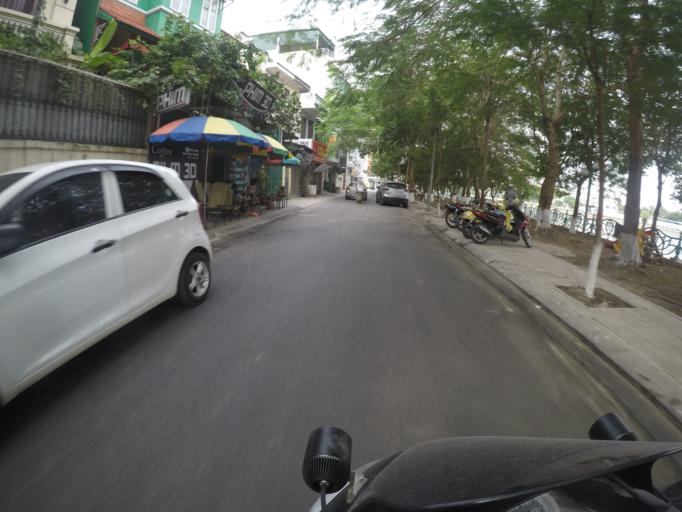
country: VN
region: Ha Noi
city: Tay Ho
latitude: 21.0721
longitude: 105.8144
